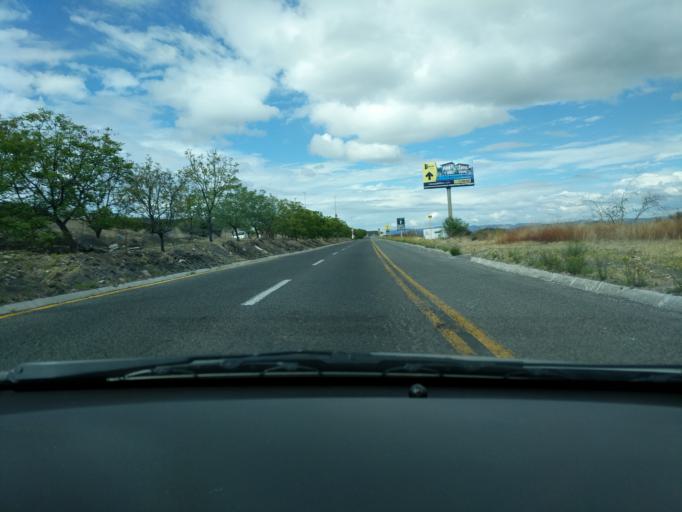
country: MX
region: Queretaro
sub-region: El Marques
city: La Pradera
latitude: 20.6650
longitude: -100.3278
